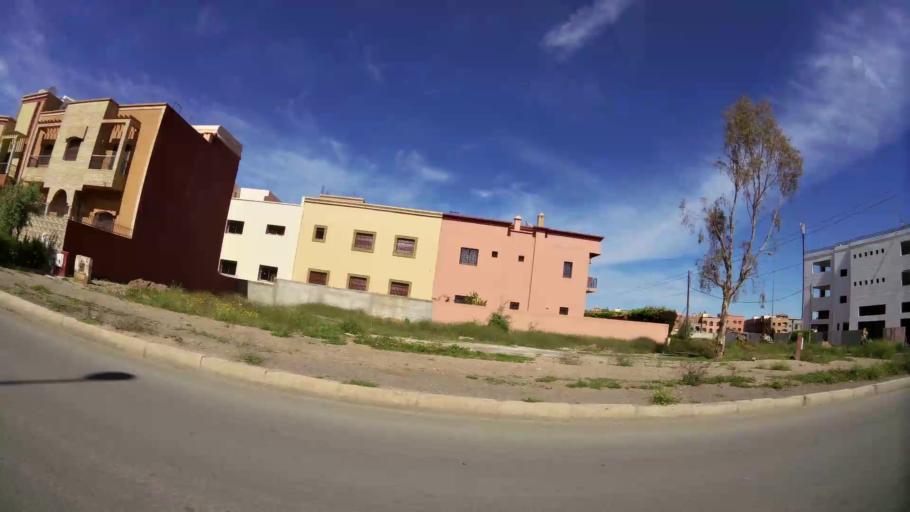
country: MA
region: Marrakech-Tensift-Al Haouz
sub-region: Marrakech
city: Marrakesh
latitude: 31.6427
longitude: -8.0427
